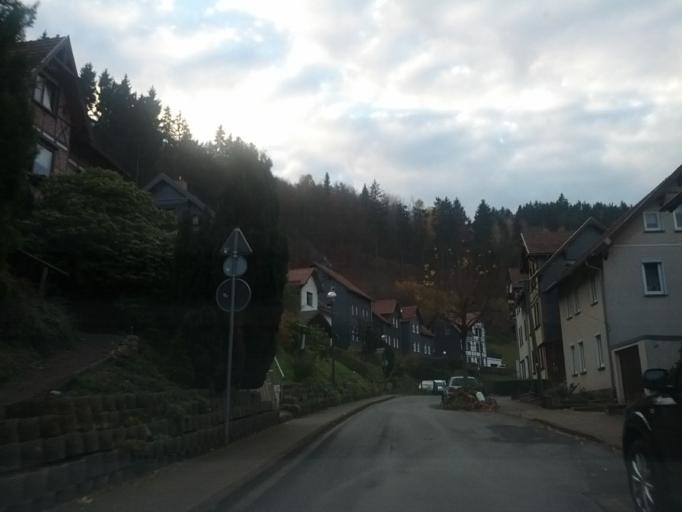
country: DE
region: Thuringia
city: Ruhla
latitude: 50.8895
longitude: 10.3575
